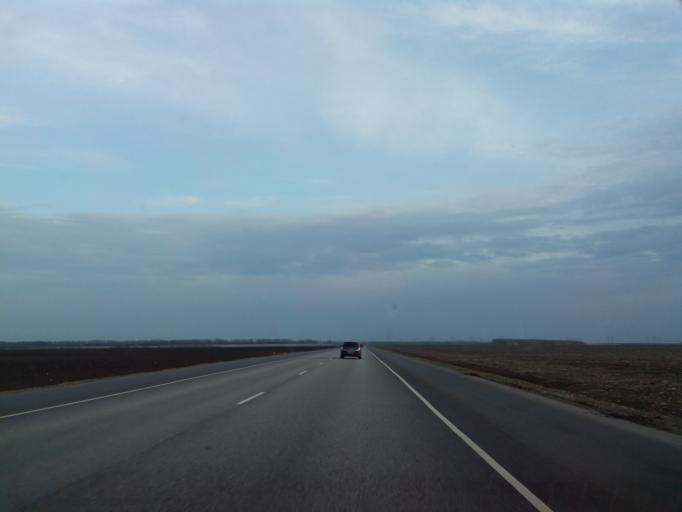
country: RU
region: Rjazan
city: Ryazhsk
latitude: 53.5697
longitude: 40.0474
